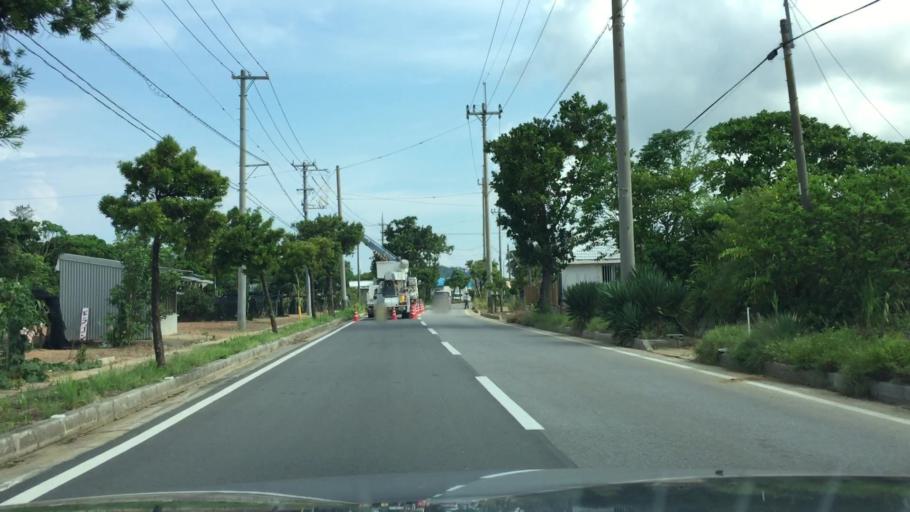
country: JP
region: Okinawa
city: Ishigaki
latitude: 24.4639
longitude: 124.2503
